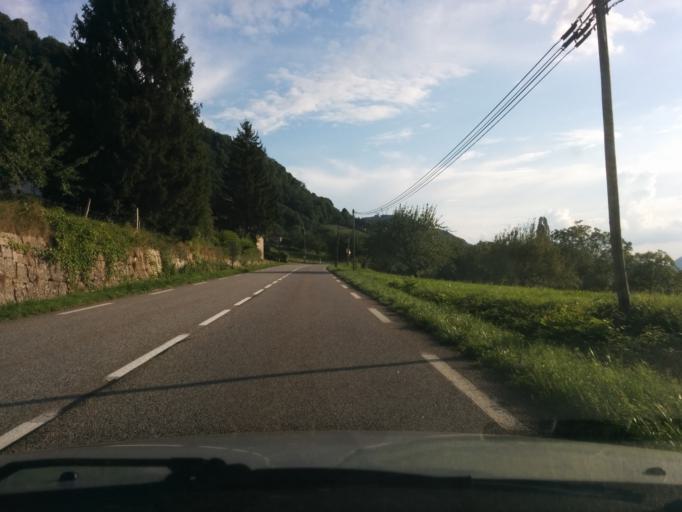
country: FR
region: Rhone-Alpes
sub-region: Departement de la Savoie
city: Saint-Beron
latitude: 45.4956
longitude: 5.7287
